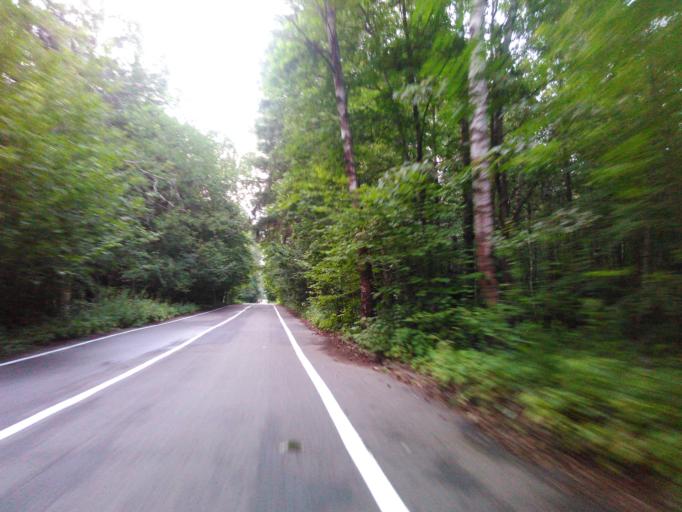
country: RU
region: Moscow
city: Babushkin
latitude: 55.8455
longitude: 37.7264
